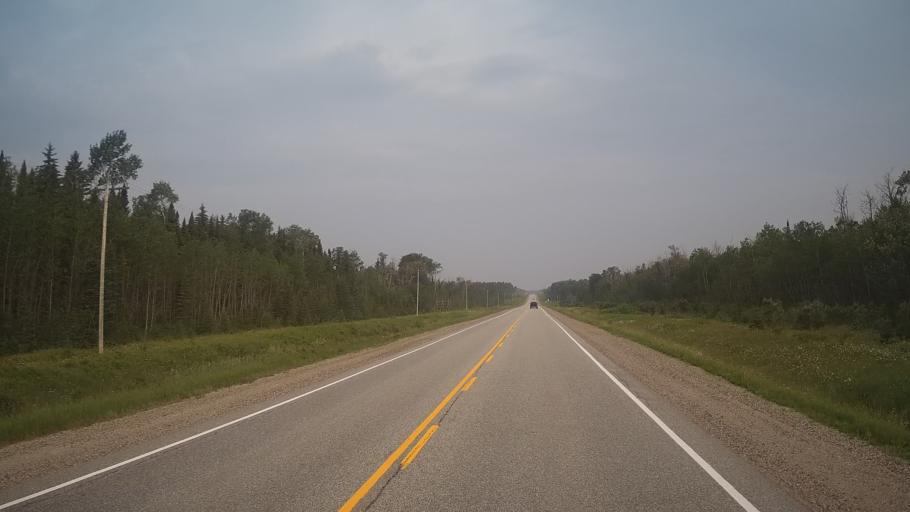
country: CA
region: Ontario
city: Hearst
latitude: 49.7277
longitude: -83.8947
